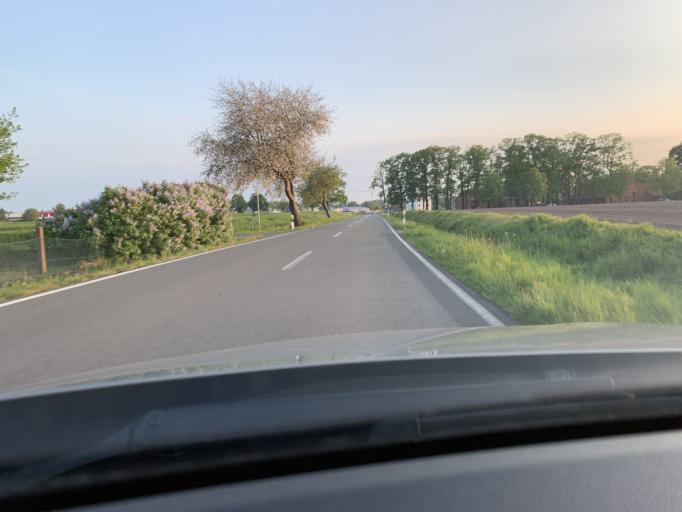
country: DE
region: North Rhine-Westphalia
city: Rietberg
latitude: 51.7730
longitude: 8.3855
